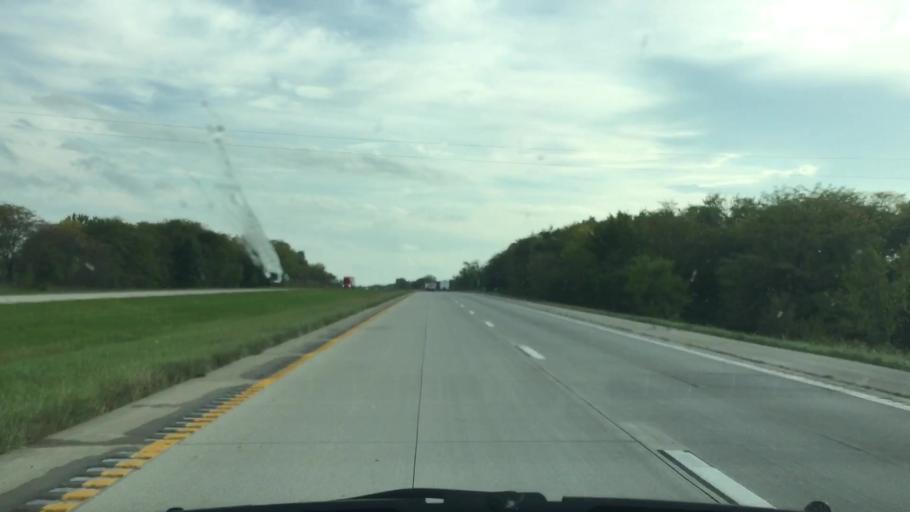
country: US
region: Missouri
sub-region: Daviess County
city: Gallatin
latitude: 40.0110
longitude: -94.0965
